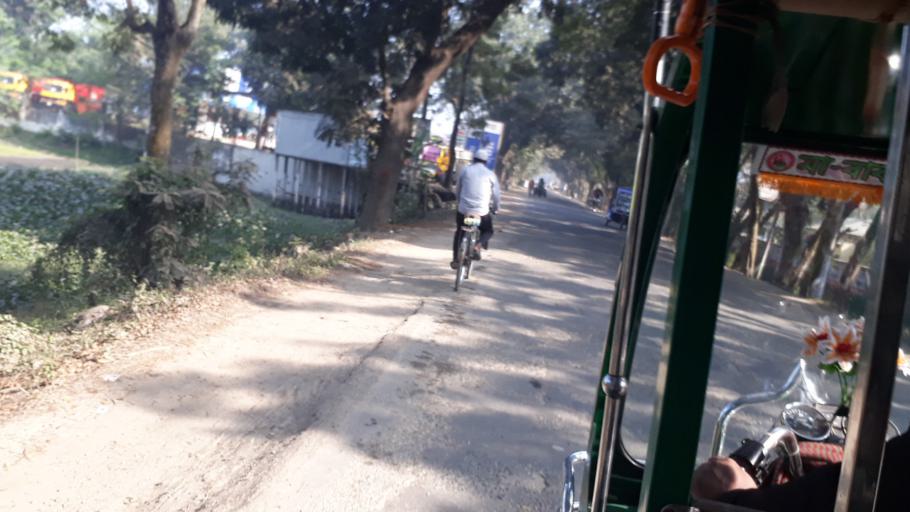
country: BD
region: Khulna
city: Kushtia
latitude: 23.8905
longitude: 89.1123
